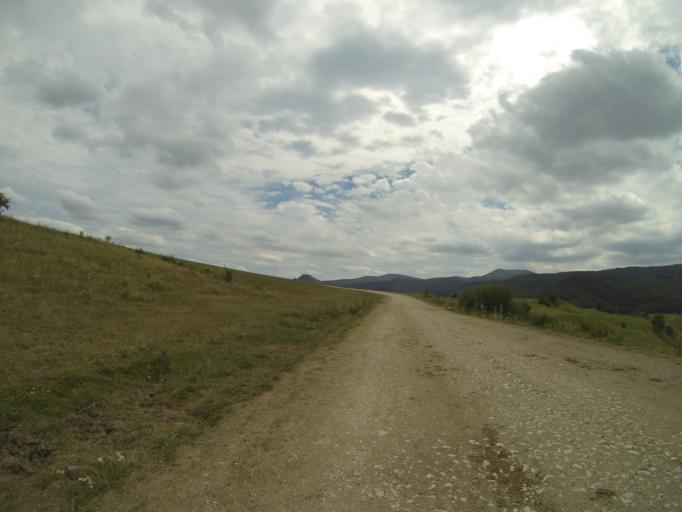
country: RO
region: Brasov
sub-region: Comuna Apata
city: Apata
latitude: 46.0276
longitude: 25.4190
